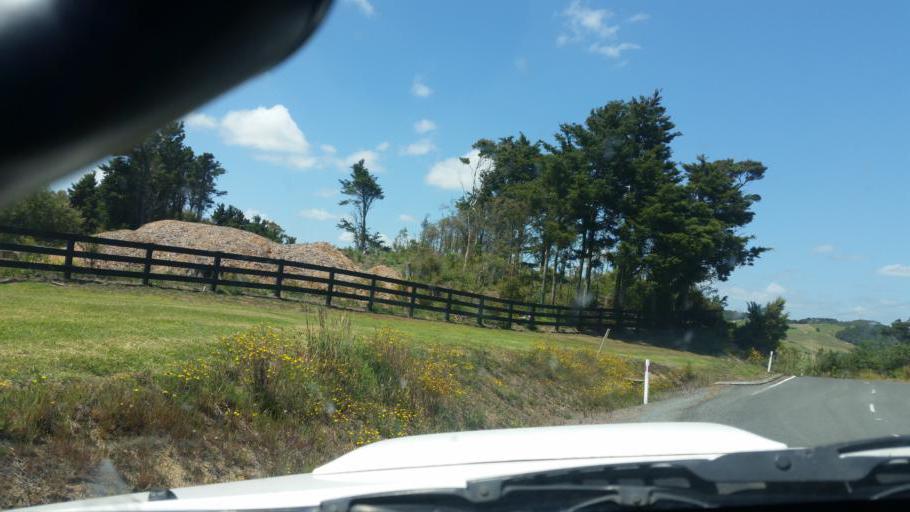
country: NZ
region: Auckland
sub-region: Auckland
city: Wellsford
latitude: -36.1405
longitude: 174.5569
